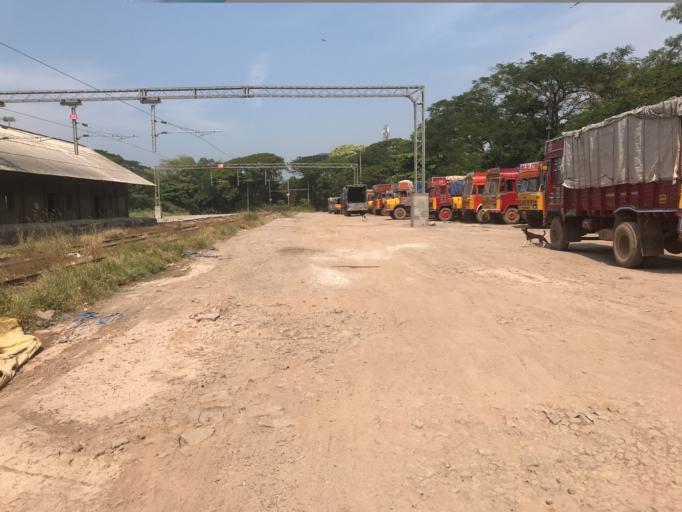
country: IN
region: Karnataka
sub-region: Dakshina Kannada
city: Ullal
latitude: 12.8557
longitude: 74.8347
